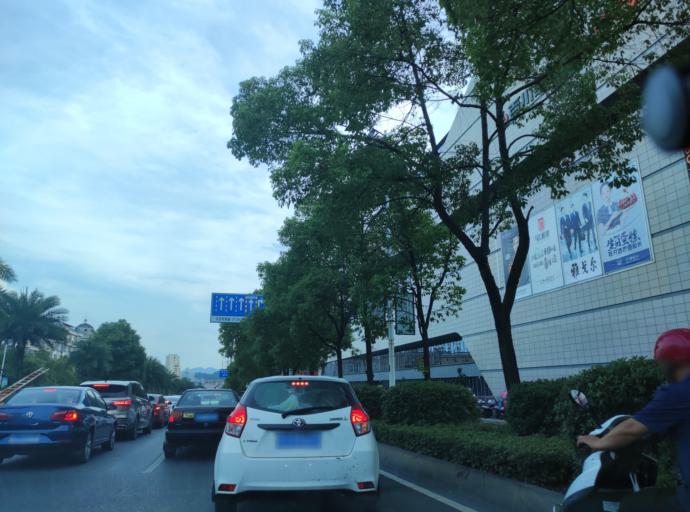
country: CN
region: Jiangxi Sheng
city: Pingxiang
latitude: 27.6353
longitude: 113.8695
